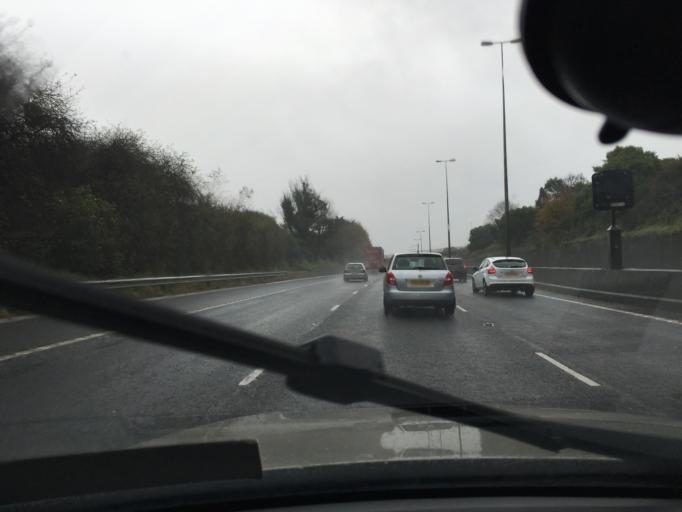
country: GB
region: Northern Ireland
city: Carnmoney
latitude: 54.6670
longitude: -5.9555
